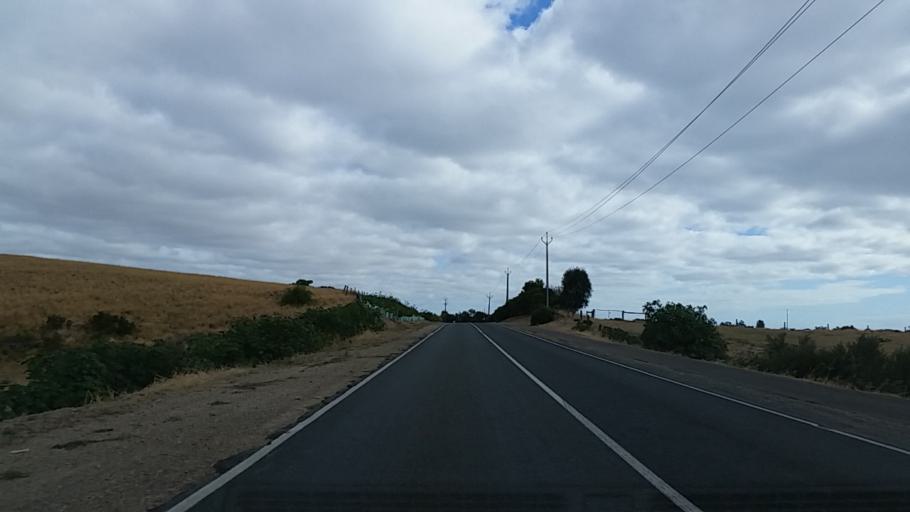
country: AU
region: South Australia
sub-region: Yankalilla
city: Normanville
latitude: -35.4327
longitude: 138.3236
